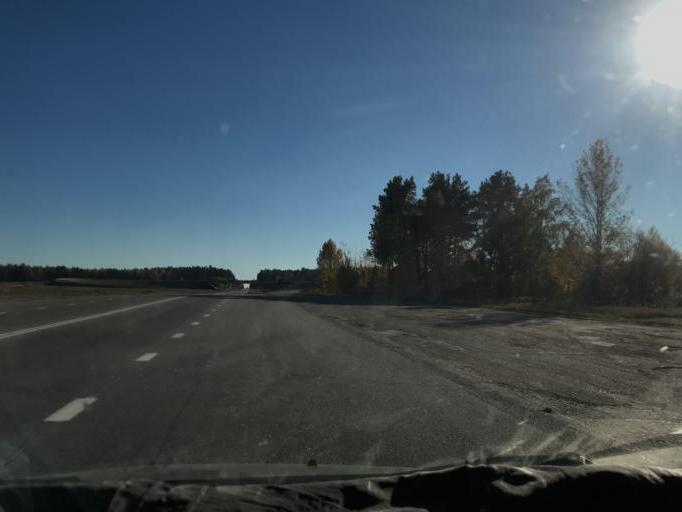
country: BY
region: Gomel
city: Kalinkavichy
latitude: 52.0774
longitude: 29.3609
